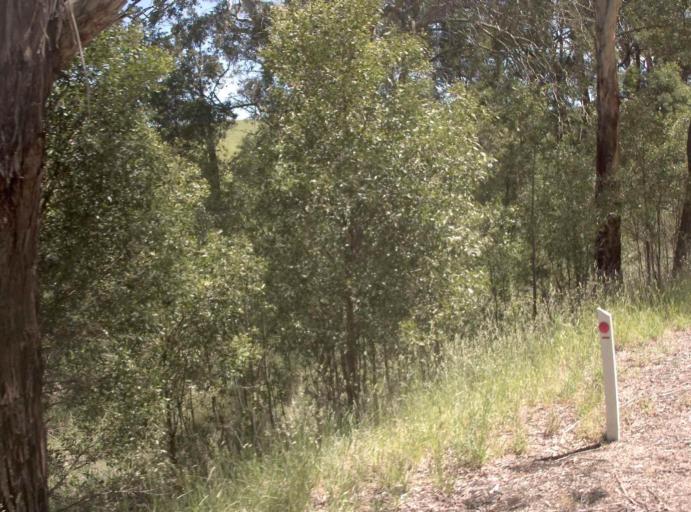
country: AU
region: Victoria
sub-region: East Gippsland
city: Lakes Entrance
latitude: -37.2168
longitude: 148.2669
